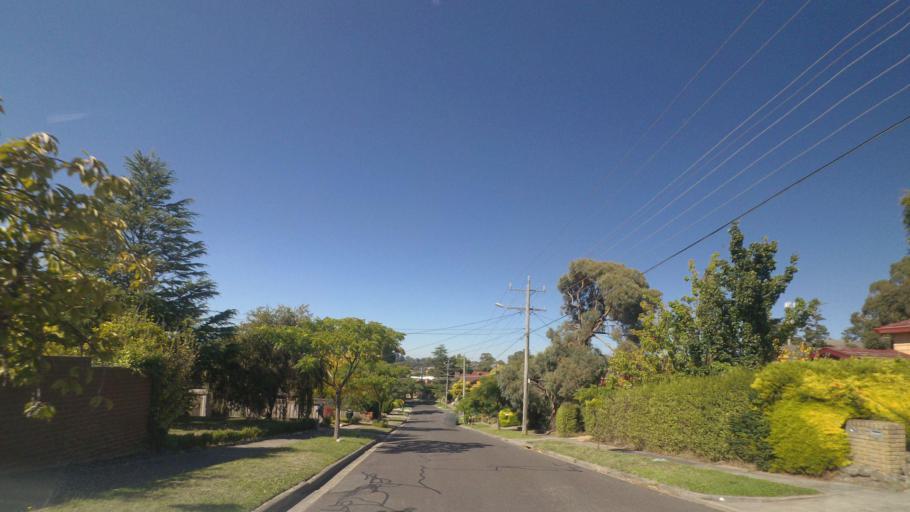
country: AU
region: Victoria
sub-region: Manningham
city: Donvale
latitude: -37.7806
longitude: 145.1666
